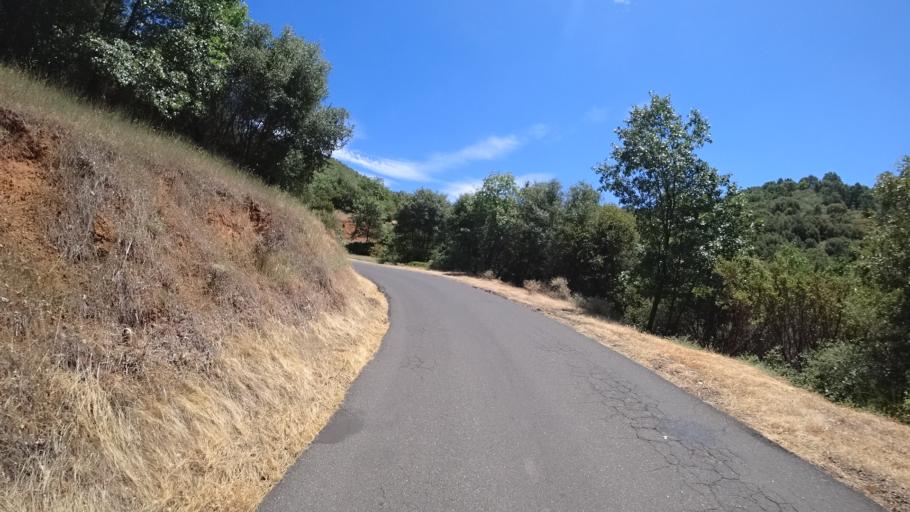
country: US
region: California
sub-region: Calaveras County
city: Forest Meadows
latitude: 38.1968
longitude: -120.4429
